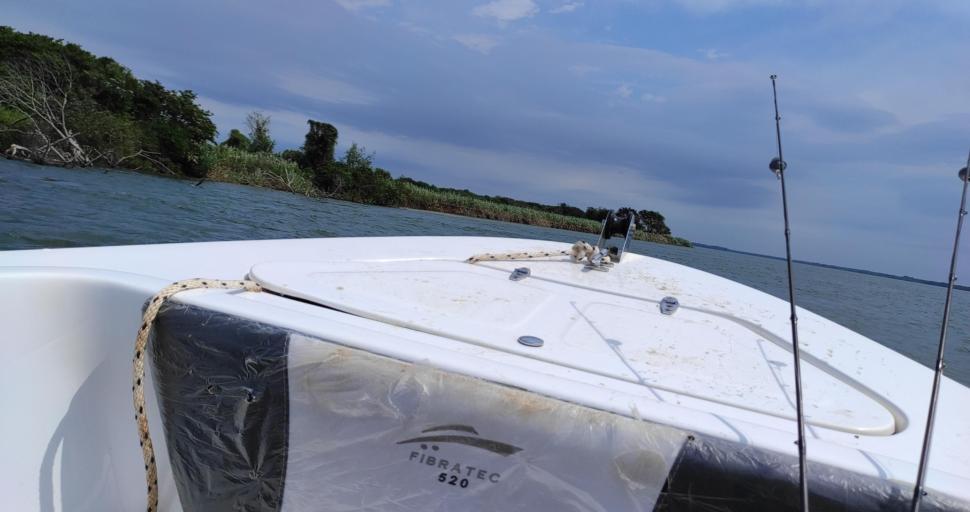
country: PY
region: Neembucu
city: Cerrito
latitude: -27.3542
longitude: -57.6761
